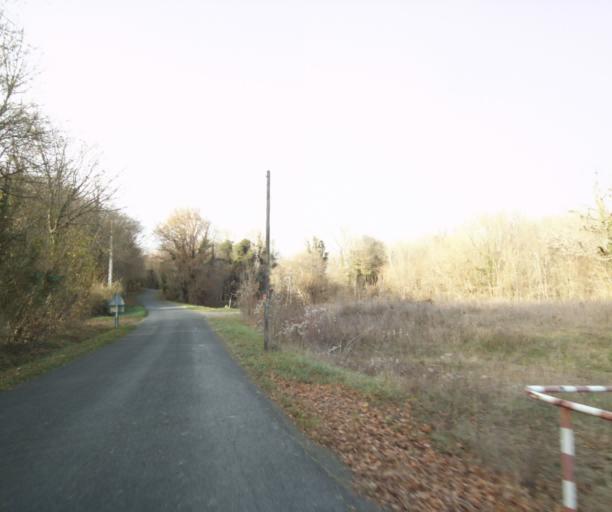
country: FR
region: Poitou-Charentes
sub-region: Departement de la Charente-Maritime
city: Saint-Hilaire-de-Villefranche
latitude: 45.8131
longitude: -0.5626
